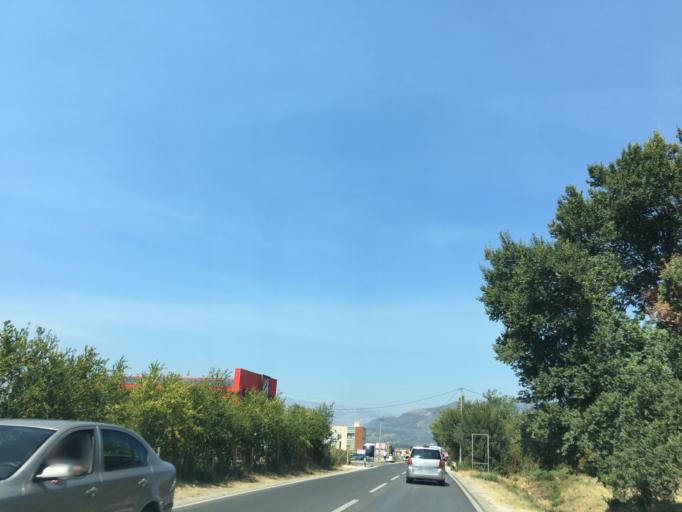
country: ME
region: Kotor
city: Kotor
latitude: 42.3749
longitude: 18.7522
